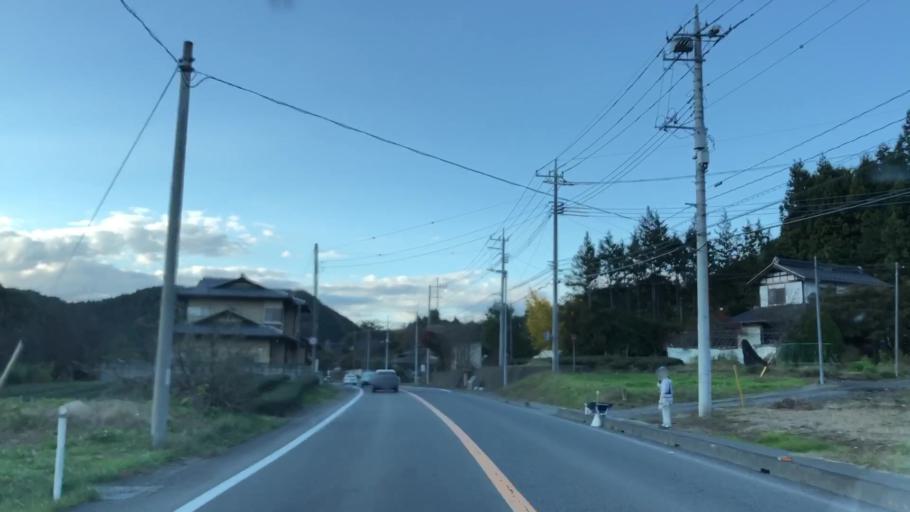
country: JP
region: Ibaraki
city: Kasama
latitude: 36.4808
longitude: 140.2943
